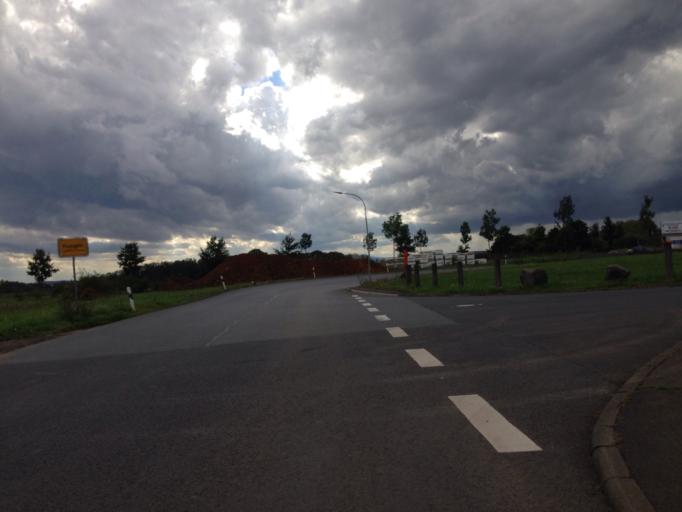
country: DE
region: Hesse
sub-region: Regierungsbezirk Giessen
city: Hungen
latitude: 50.4694
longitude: 8.9123
